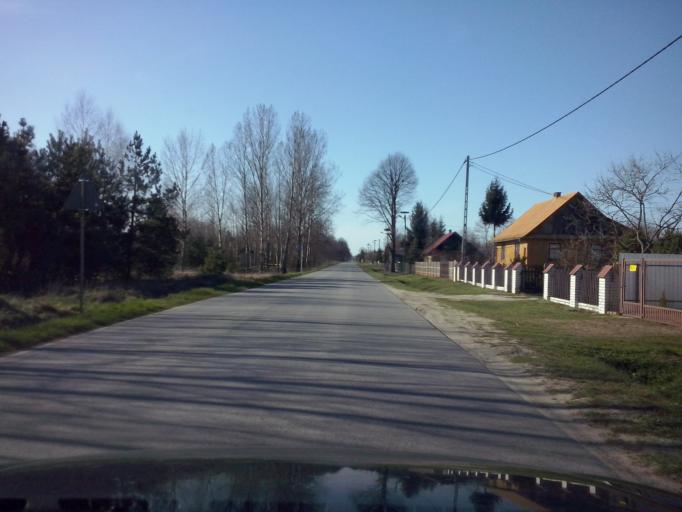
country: PL
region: Subcarpathian Voivodeship
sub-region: Powiat lezajski
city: Kurylowka
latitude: 50.3366
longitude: 22.4408
